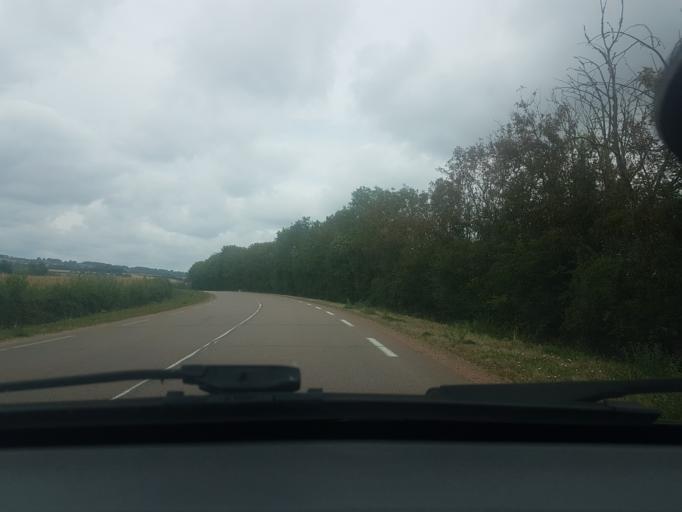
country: FR
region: Bourgogne
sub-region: Departement de la Cote-d'Or
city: Arnay-le-Duc
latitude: 47.2068
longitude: 4.3694
